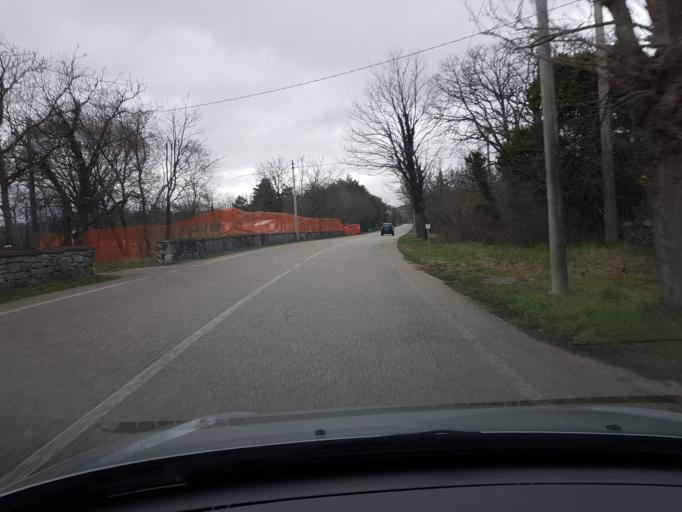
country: IT
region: Friuli Venezia Giulia
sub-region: Provincia di Trieste
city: Santa Croce
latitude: 45.7527
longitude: 13.7133
